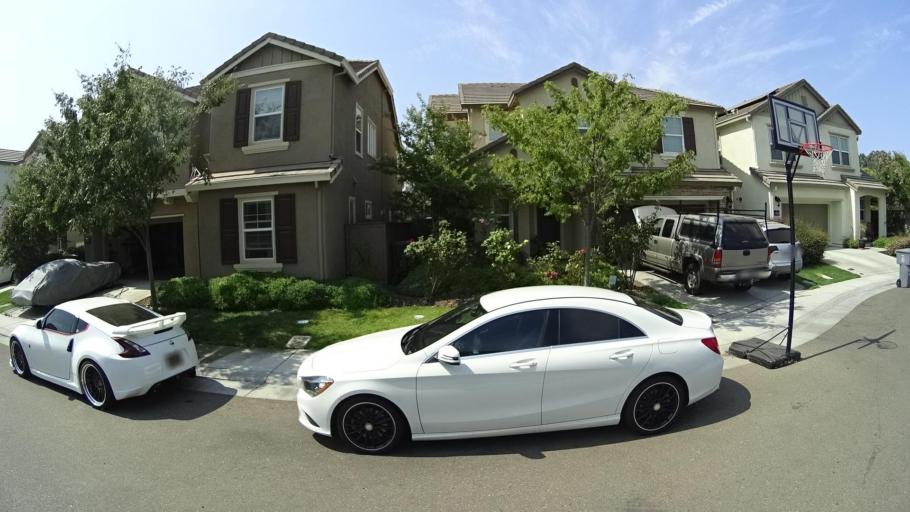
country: US
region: California
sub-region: Placer County
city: Rocklin
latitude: 38.7871
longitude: -121.2309
